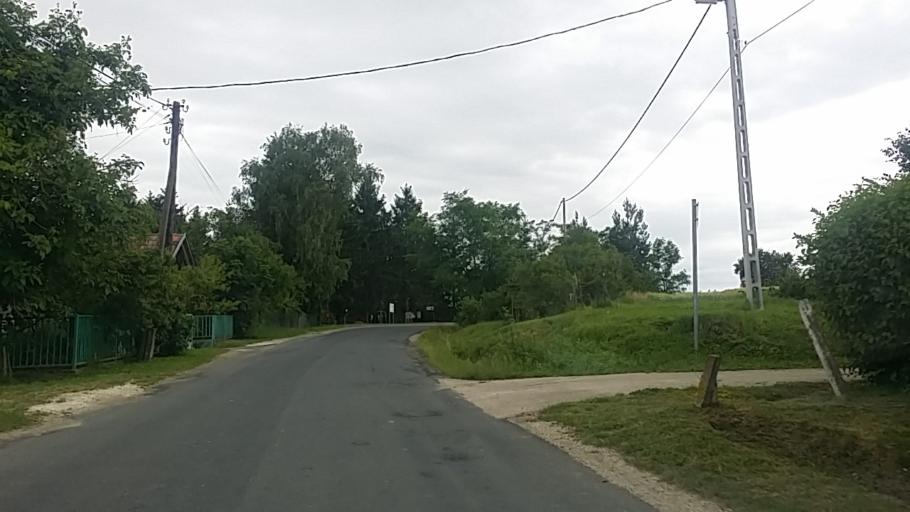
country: SI
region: Hodos-Hodos
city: Hodos
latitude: 46.8496
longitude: 16.4031
